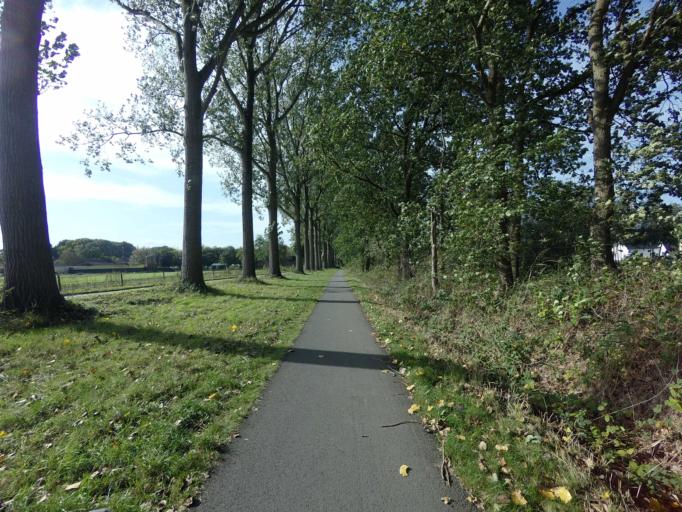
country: NL
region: North Brabant
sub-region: Gemeente Breda
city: Hoge Vucht
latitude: 51.5996
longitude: 4.8254
